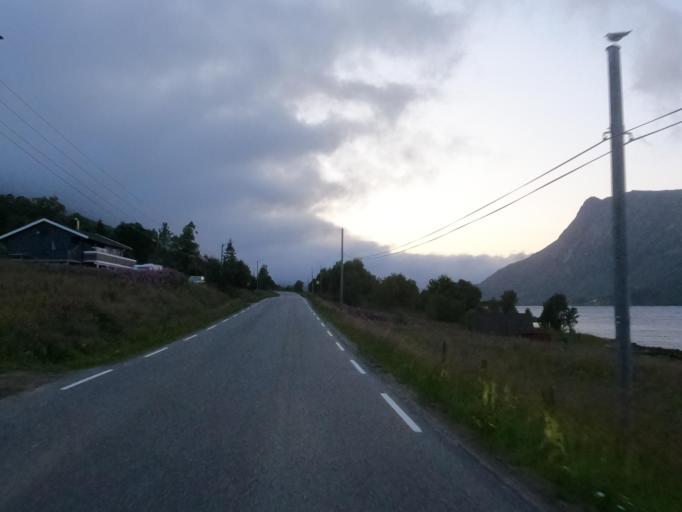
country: NO
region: Nordland
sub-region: Lodingen
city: Lodingen
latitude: 68.5734
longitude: 15.7954
